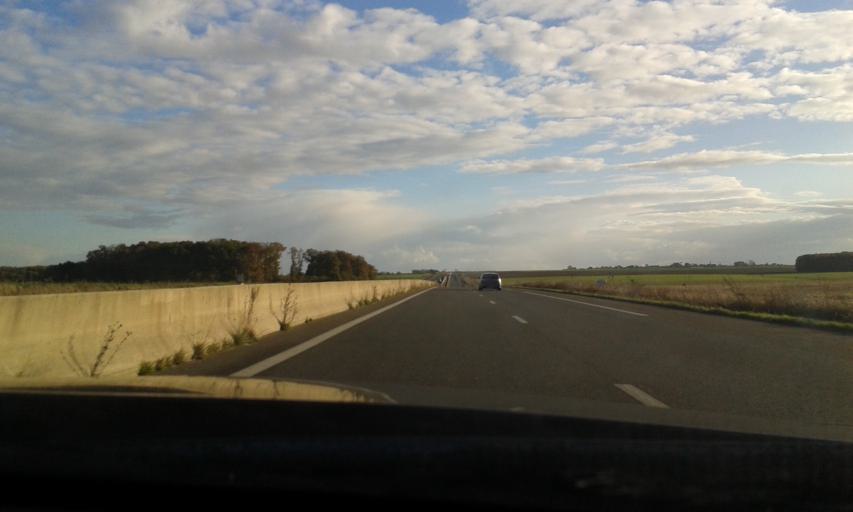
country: FR
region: Centre
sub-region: Departement d'Eure-et-Loir
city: Bailleau-l'Eveque
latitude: 48.5771
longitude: 1.4324
